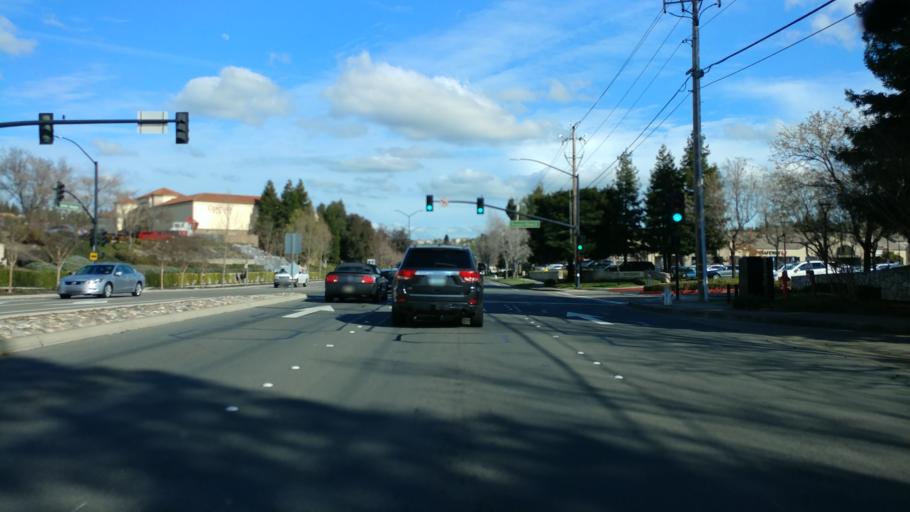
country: US
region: California
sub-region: Contra Costa County
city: Blackhawk
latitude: 37.7989
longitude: -121.9200
